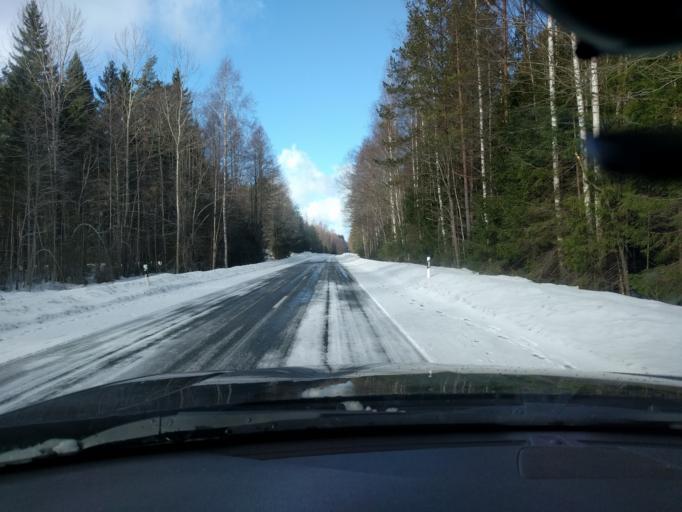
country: EE
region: Harju
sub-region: Anija vald
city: Kehra
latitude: 59.2143
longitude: 25.4947
